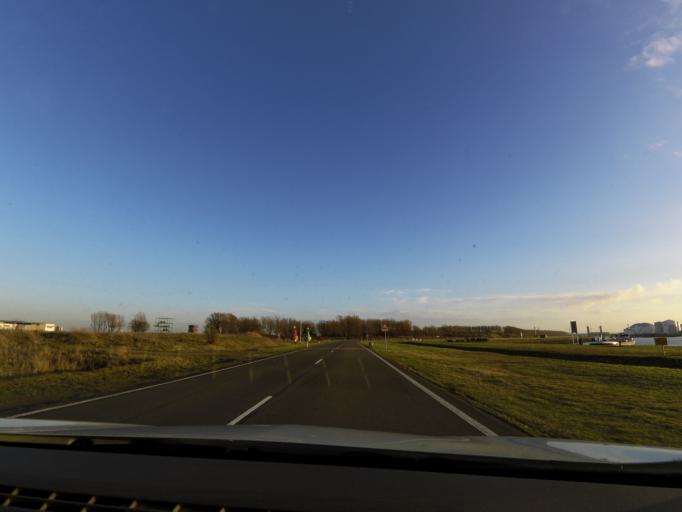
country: NL
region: South Holland
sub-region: Gemeente Maassluis
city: Maassluis
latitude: 51.9239
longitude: 4.2175
